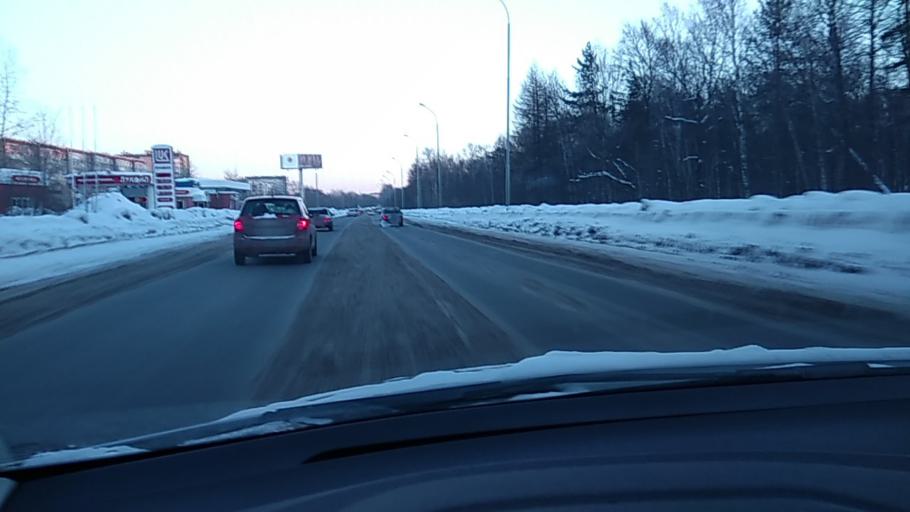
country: RU
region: Sverdlovsk
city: Sovkhoznyy
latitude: 56.8025
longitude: 60.5429
